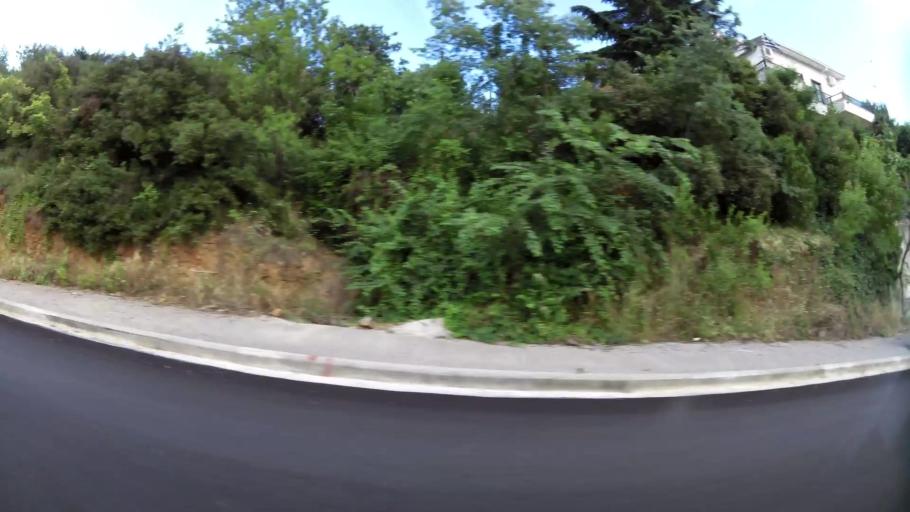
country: GR
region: Central Macedonia
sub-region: Nomos Thessalonikis
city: Pefka
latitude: 40.6583
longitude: 22.9975
